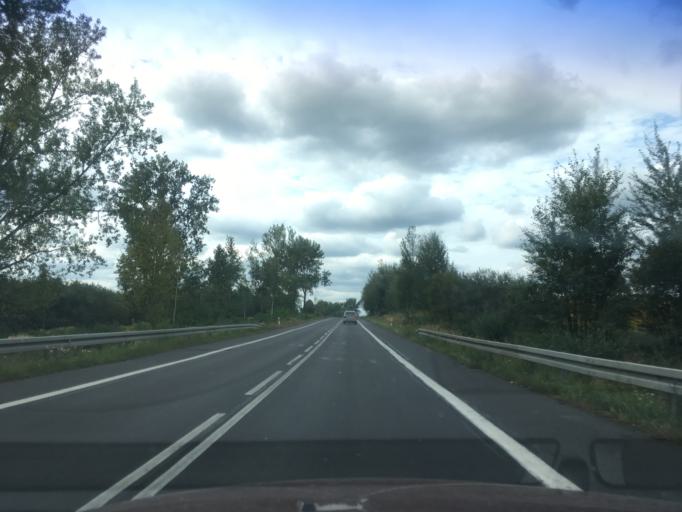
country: PL
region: Lower Silesian Voivodeship
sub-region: Powiat lubanski
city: Luban
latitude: 51.0921
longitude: 15.3202
